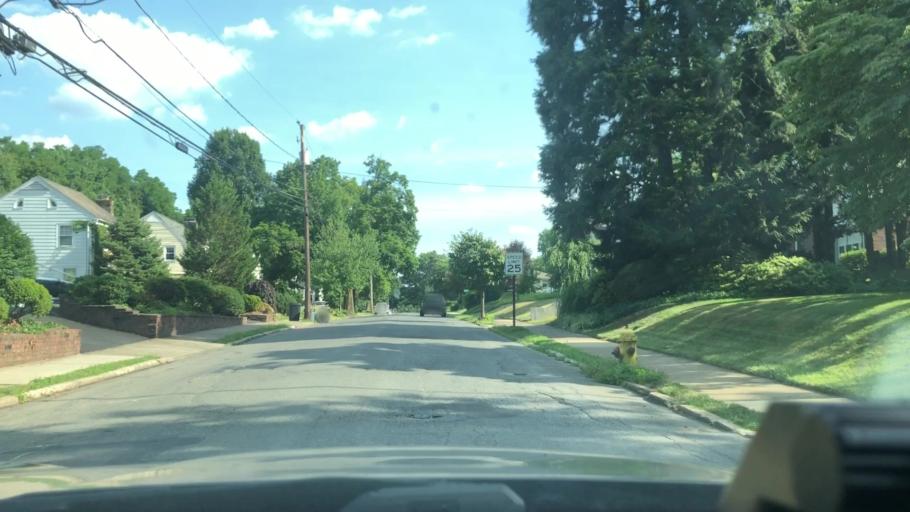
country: US
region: Pennsylvania
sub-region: Lehigh County
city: Fountain Hill
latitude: 40.6294
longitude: -75.4090
